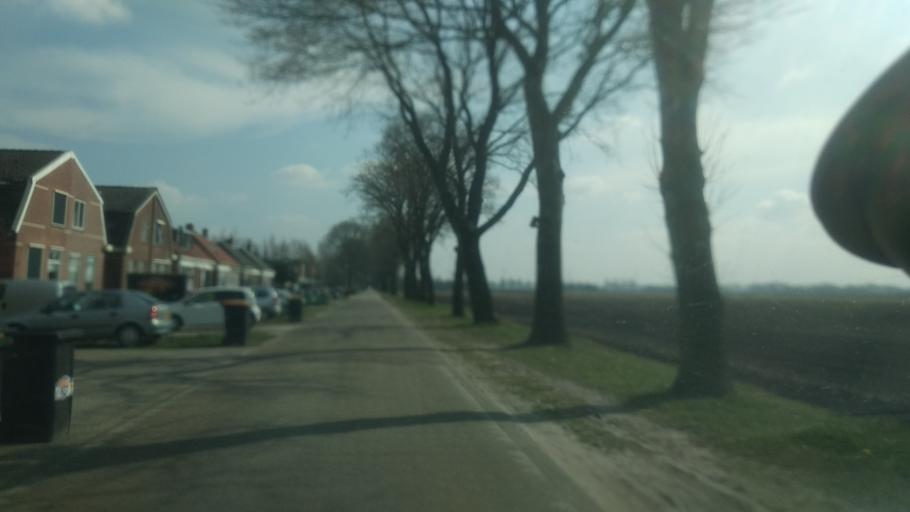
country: NL
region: Groningen
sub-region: Gemeente Stadskanaal
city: Stadskanaal
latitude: 52.9976
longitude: 6.9256
